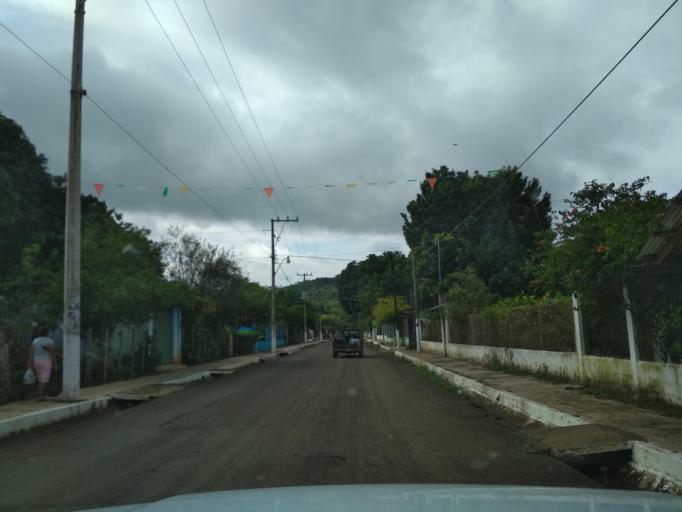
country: MX
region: Veracruz
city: Catemaco
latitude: 18.3761
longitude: -95.1242
